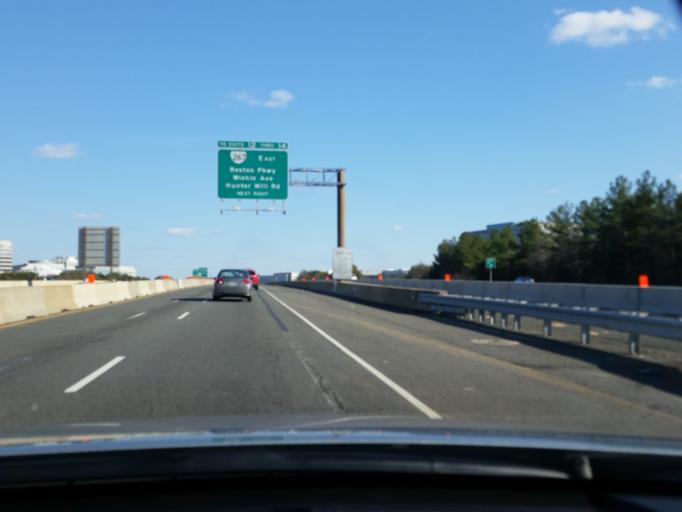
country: US
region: Virginia
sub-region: Fairfax County
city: Floris
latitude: 38.9583
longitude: -77.4087
